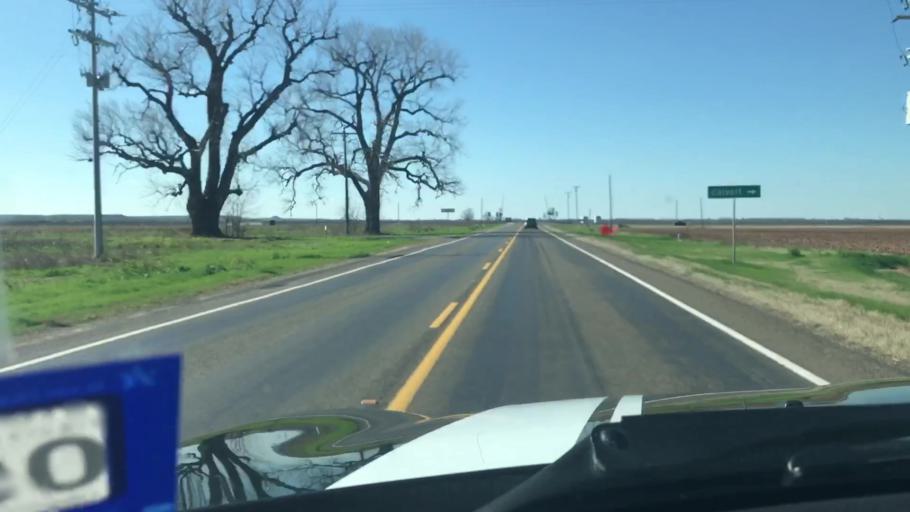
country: US
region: Texas
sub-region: Robertson County
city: Hearne
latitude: 30.8736
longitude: -96.6586
